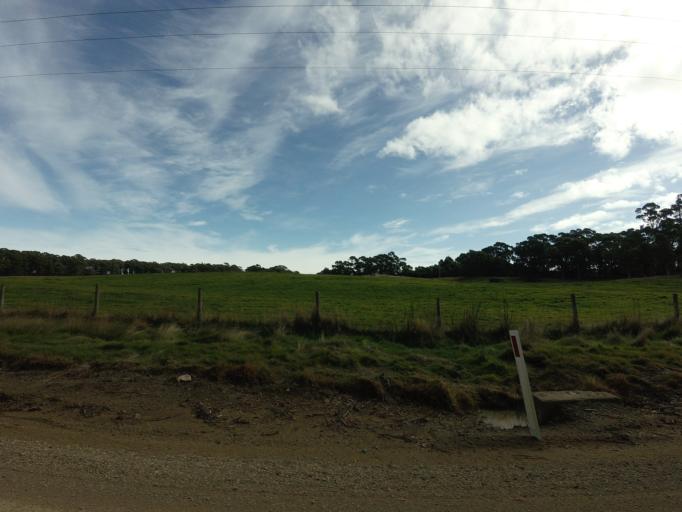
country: AU
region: Tasmania
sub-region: Clarence
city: Sandford
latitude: -43.1655
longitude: 147.7682
